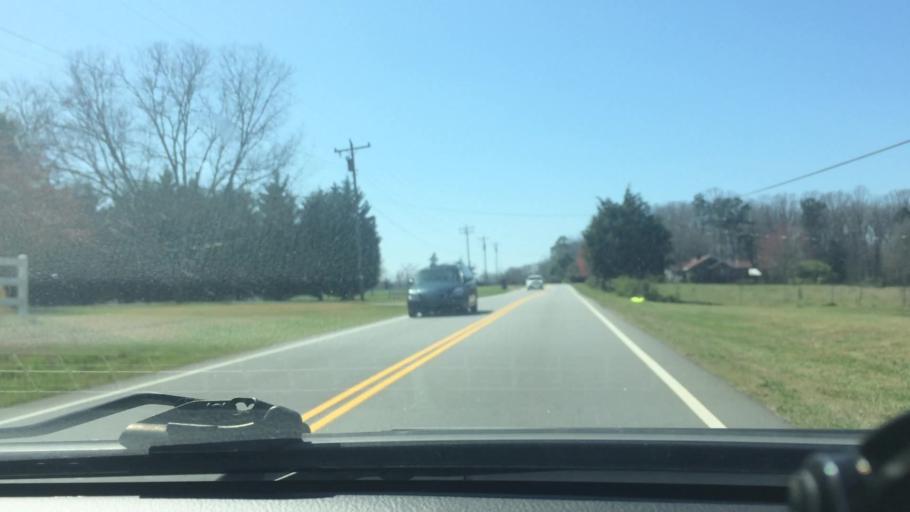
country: US
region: South Carolina
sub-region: Anderson County
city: Powdersville
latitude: 34.7889
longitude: -82.4951
